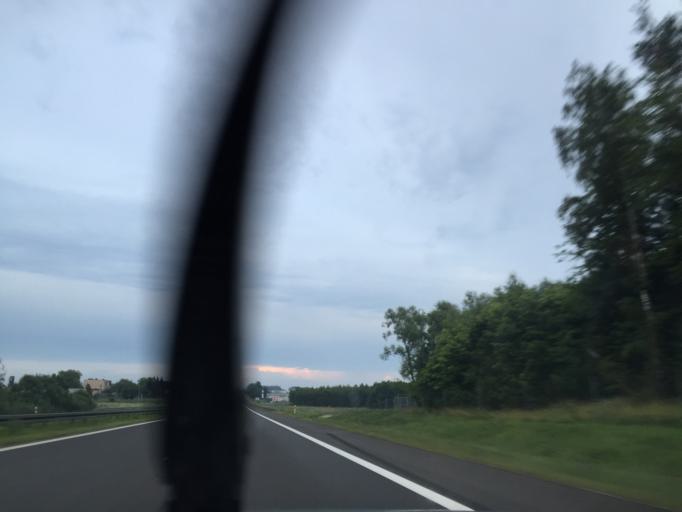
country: PL
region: Podlasie
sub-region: Powiat bialostocki
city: Choroszcz
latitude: 53.1551
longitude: 23.0217
